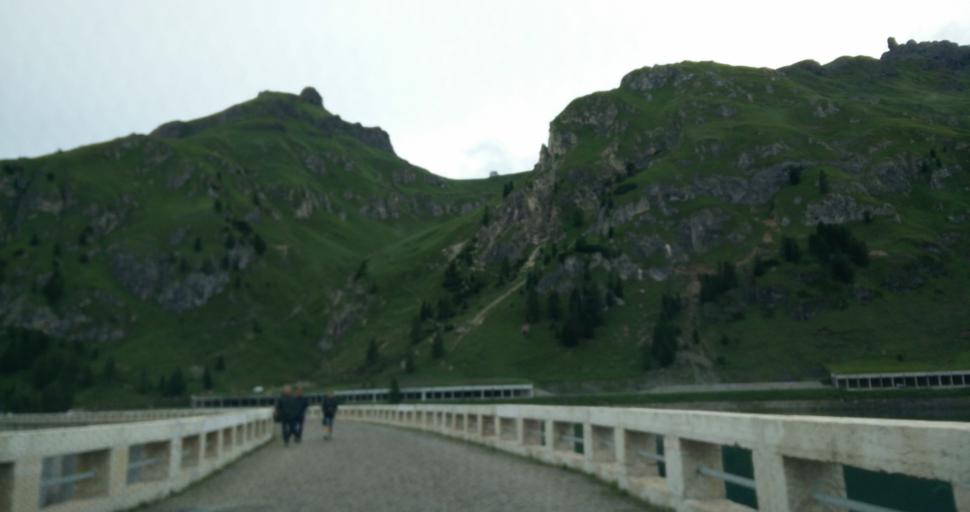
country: IT
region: Trentino-Alto Adige
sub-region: Bolzano
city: Corvara in Badia
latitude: 46.4599
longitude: 11.8645
